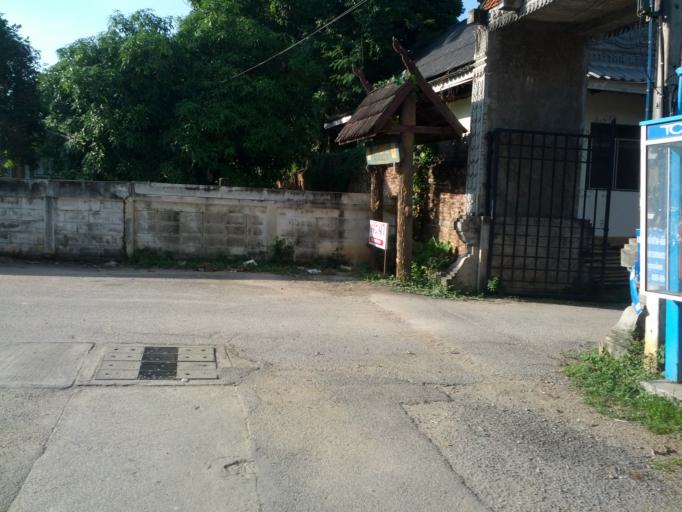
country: TH
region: Lampang
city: Lampang
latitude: 18.3026
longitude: 99.5013
